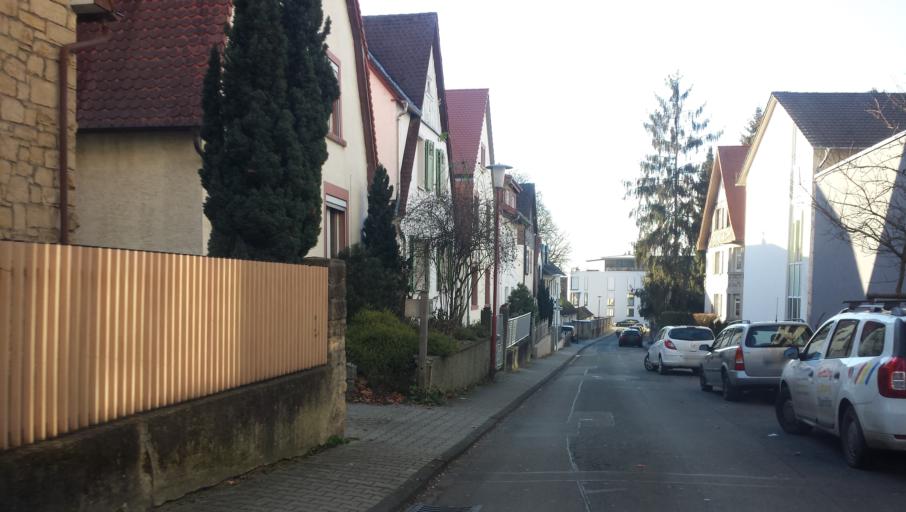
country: DE
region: Hesse
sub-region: Regierungsbezirk Darmstadt
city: Heppenheim an der Bergstrasse
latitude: 49.6400
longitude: 8.6450
